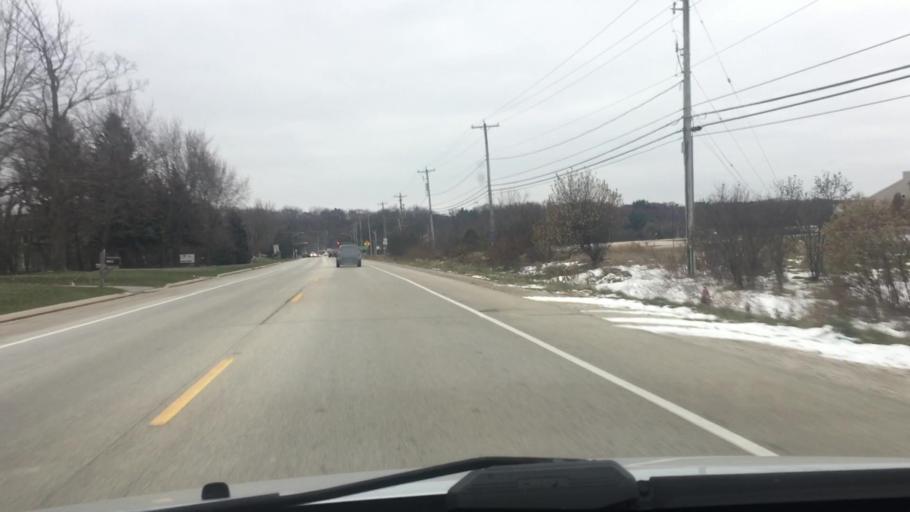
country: US
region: Wisconsin
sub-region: Waukesha County
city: Hartland
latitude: 43.0800
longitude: -88.3634
